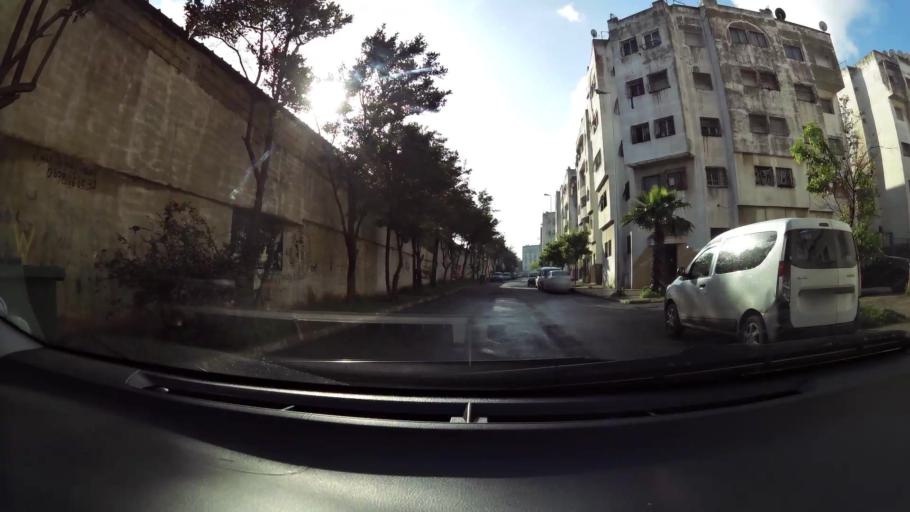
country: MA
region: Grand Casablanca
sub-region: Mediouna
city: Tit Mellil
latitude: 33.6003
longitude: -7.5232
